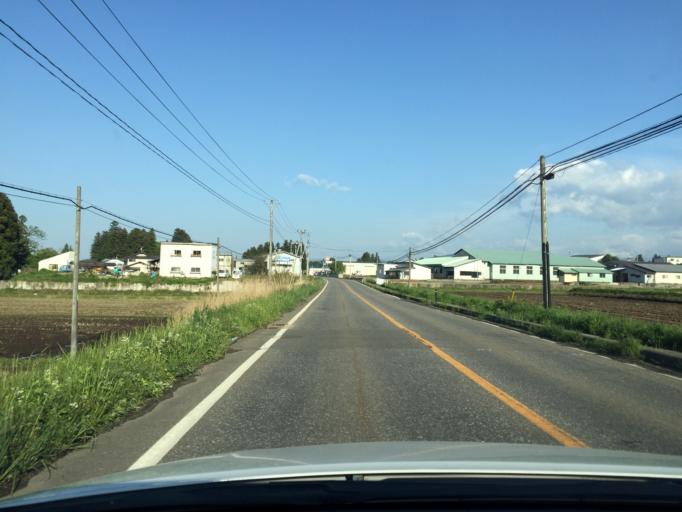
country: JP
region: Fukushima
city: Kitakata
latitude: 37.6585
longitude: 139.9228
